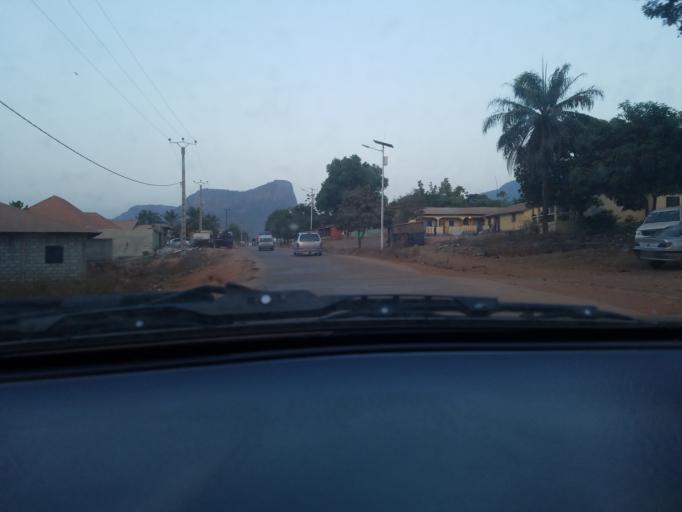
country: GN
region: Kindia
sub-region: Prefecture de Dubreka
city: Dubreka
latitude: 9.7881
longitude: -13.4996
